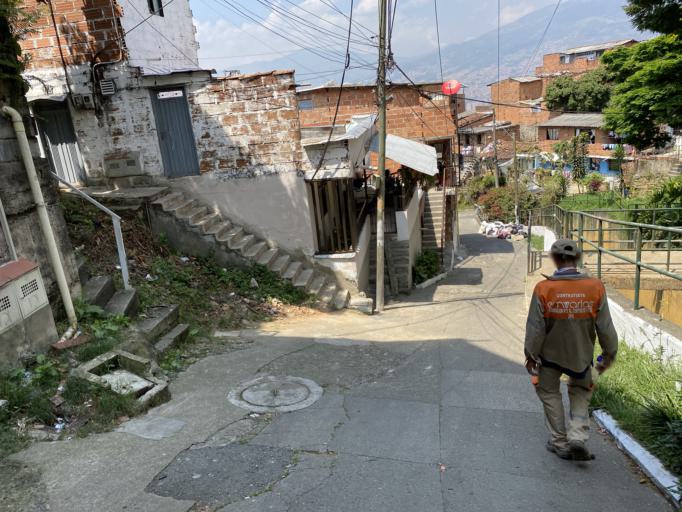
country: CO
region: Antioquia
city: Medellin
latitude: 6.2677
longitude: -75.5433
